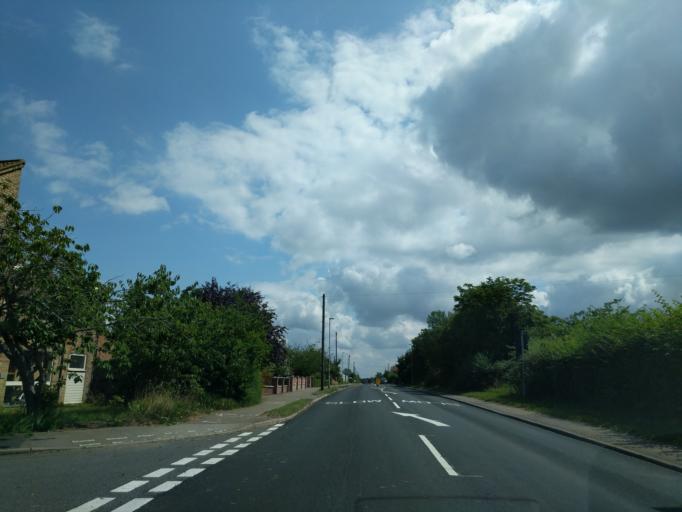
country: GB
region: England
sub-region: Cambridgeshire
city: Isleham
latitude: 52.3108
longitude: 0.3968
